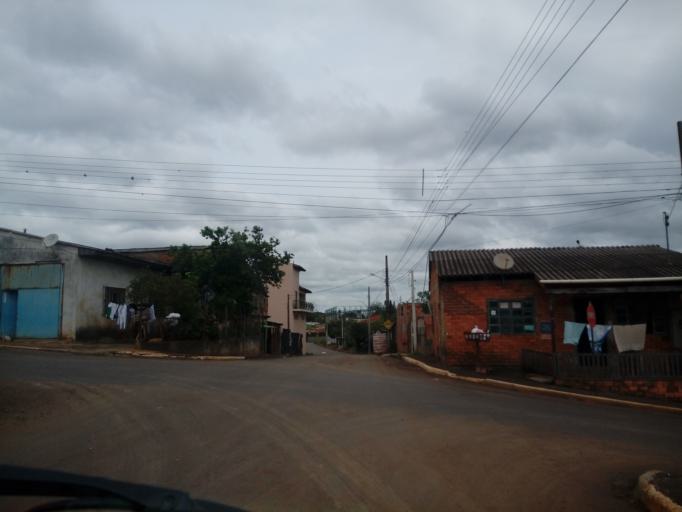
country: BR
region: Santa Catarina
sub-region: Chapeco
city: Chapeco
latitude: -27.0698
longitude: -52.6199
